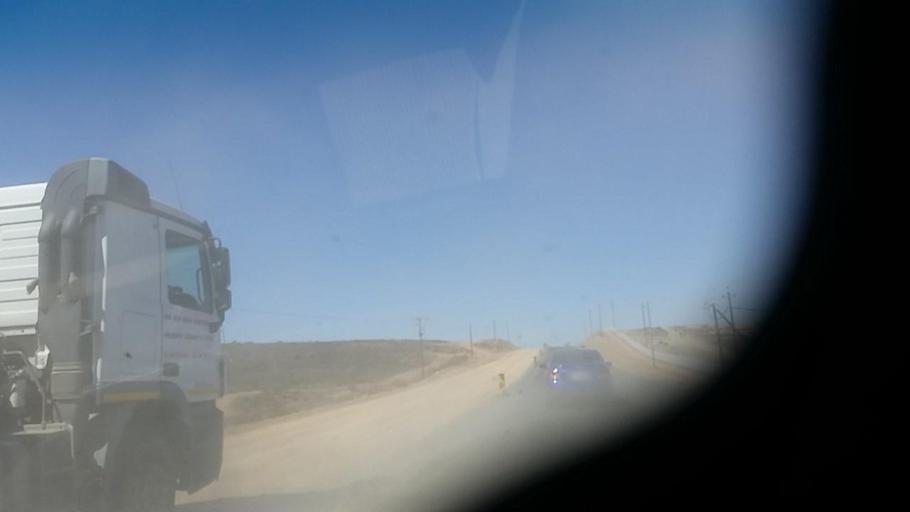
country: ZA
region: Western Cape
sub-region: Eden District Municipality
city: Oudtshoorn
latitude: -33.5906
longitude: 22.2469
